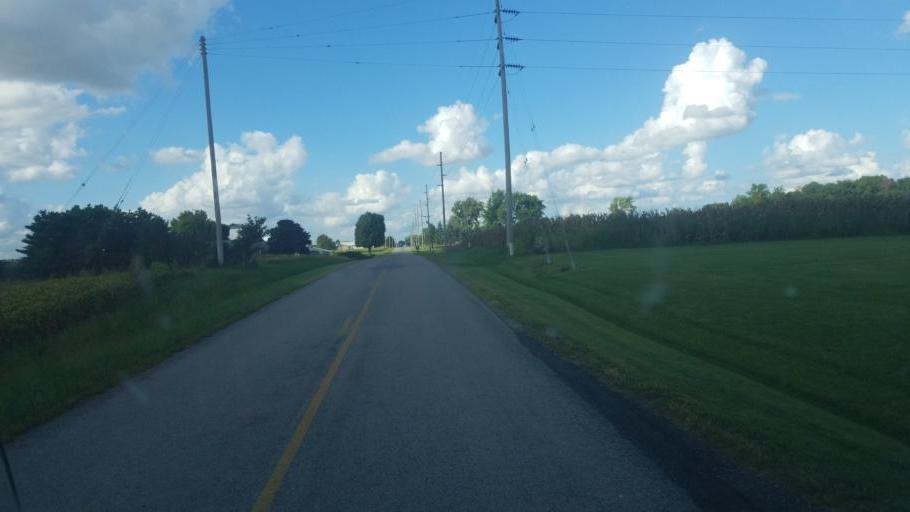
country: US
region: Ohio
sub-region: Hardin County
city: Kenton
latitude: 40.6959
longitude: -83.6921
